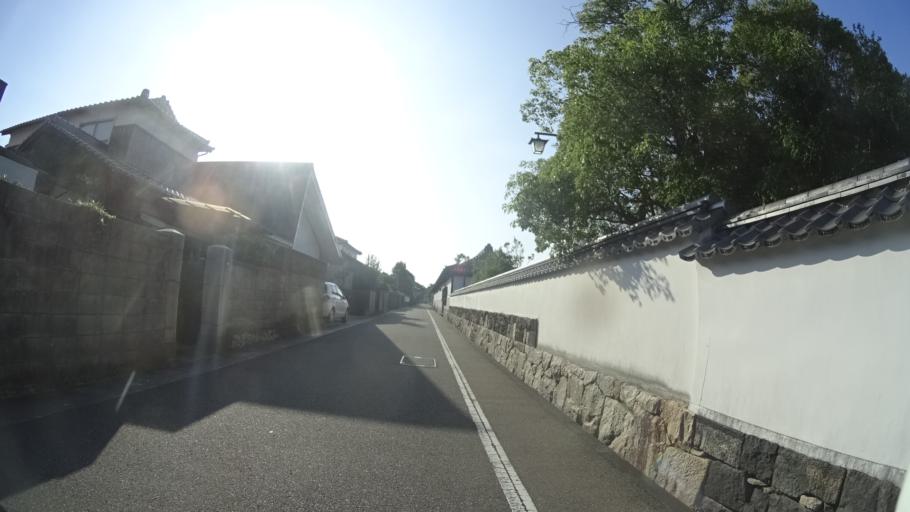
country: JP
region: Yamaguchi
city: Hagi
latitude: 34.4126
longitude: 131.3909
